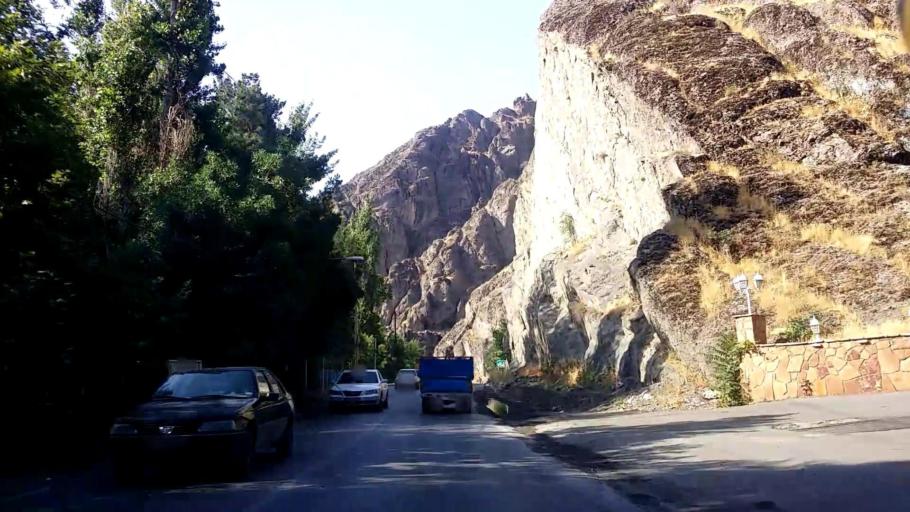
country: IR
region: Alborz
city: Karaj
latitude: 35.8811
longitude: 51.0416
